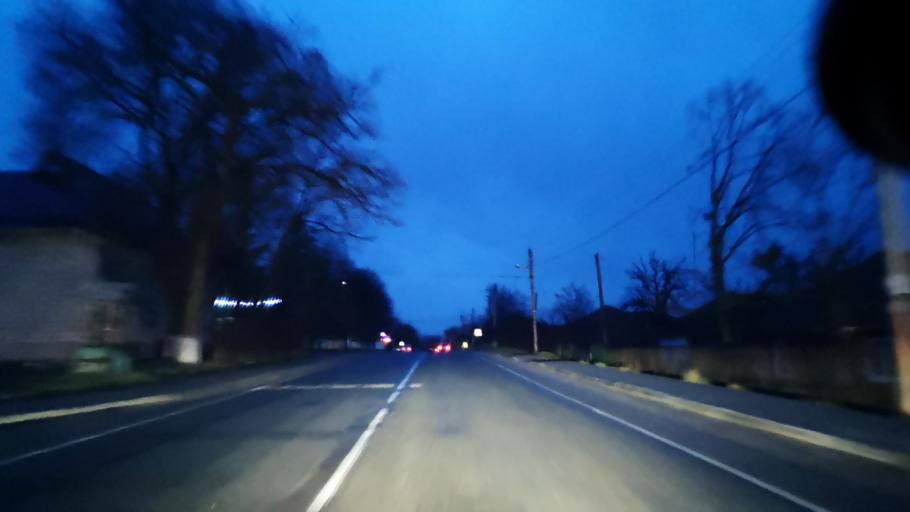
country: MD
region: Orhei
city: Orhei
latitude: 47.4386
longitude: 28.7963
